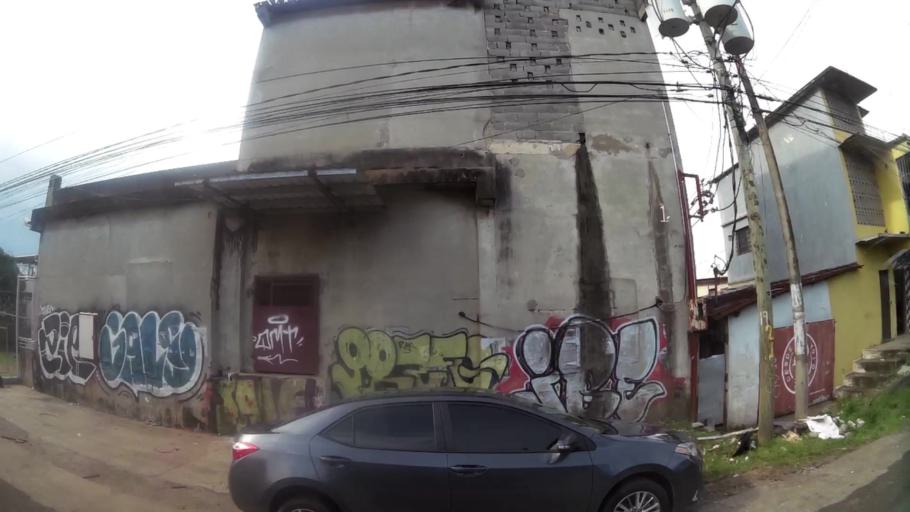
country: PA
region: Panama
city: La Chorrera
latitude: 8.8773
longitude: -79.7841
